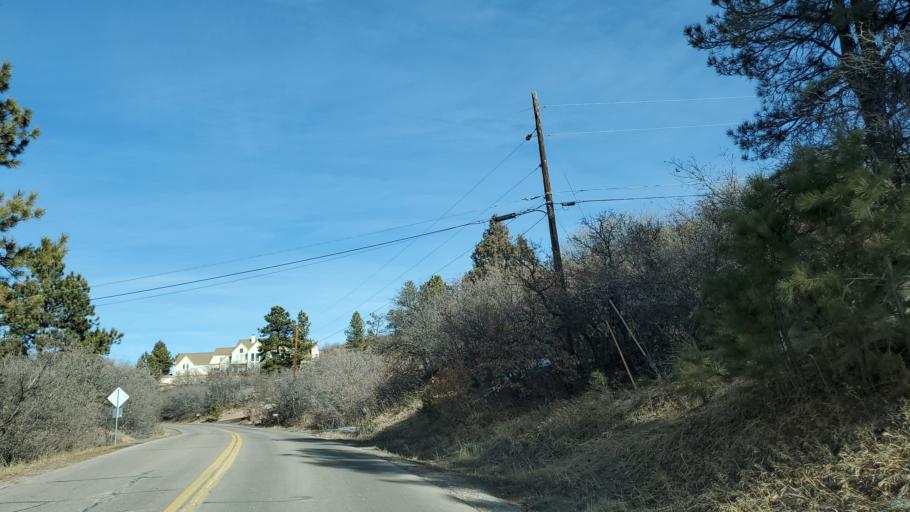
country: US
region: Colorado
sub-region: Douglas County
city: Castle Pines
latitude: 39.4389
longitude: -104.8732
